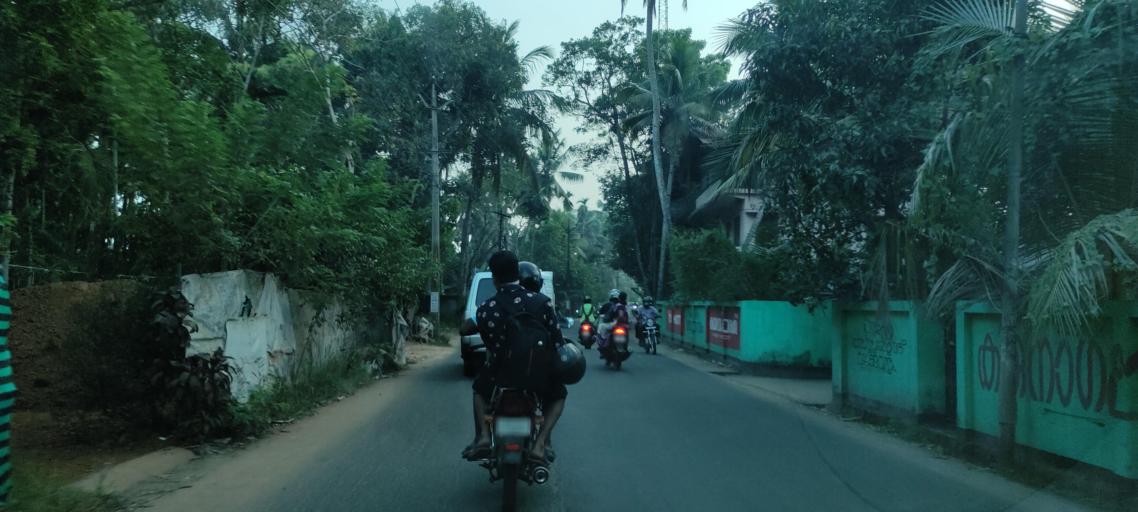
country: IN
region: Kerala
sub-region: Alappuzha
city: Kayankulam
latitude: 9.1280
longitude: 76.5030
